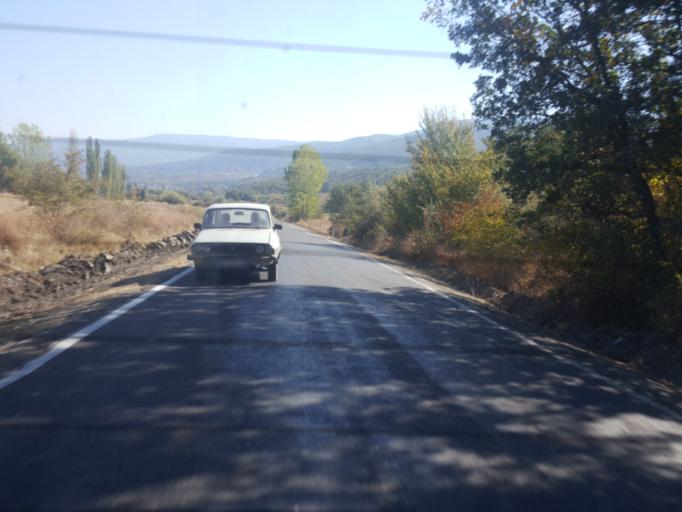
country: TR
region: Kastamonu
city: Tosya
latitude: 40.9862
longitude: 34.0858
